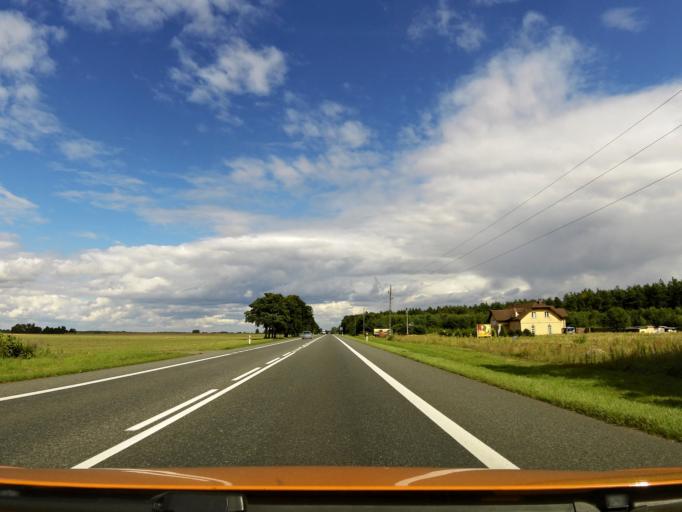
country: PL
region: West Pomeranian Voivodeship
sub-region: Powiat goleniowski
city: Osina
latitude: 53.6350
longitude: 15.0294
